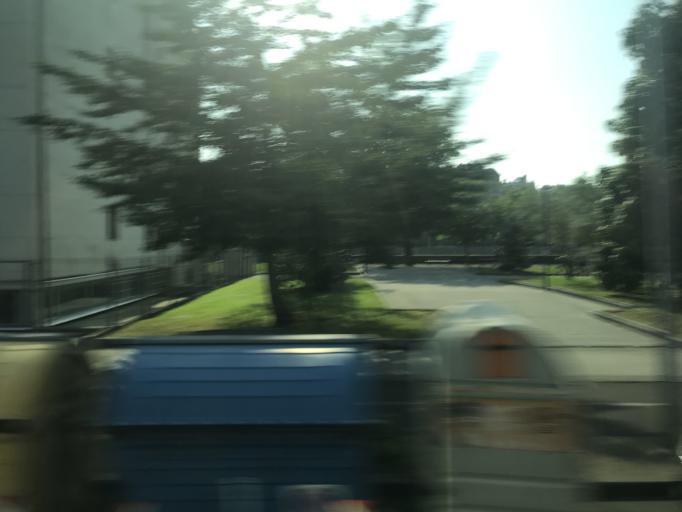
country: ES
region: Basque Country
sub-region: Provincia de Guipuzcoa
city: San Sebastian
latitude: 43.3147
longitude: -1.9776
